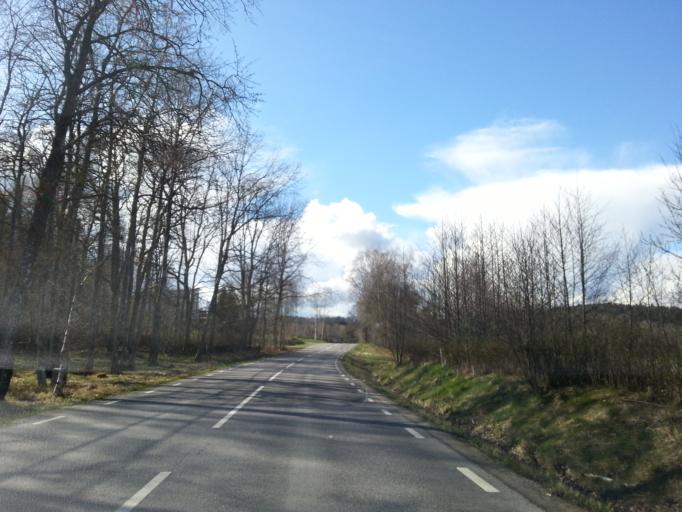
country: SE
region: Vaestra Goetaland
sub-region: Kungalvs Kommun
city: Diserod
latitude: 57.9379
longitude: 12.0275
